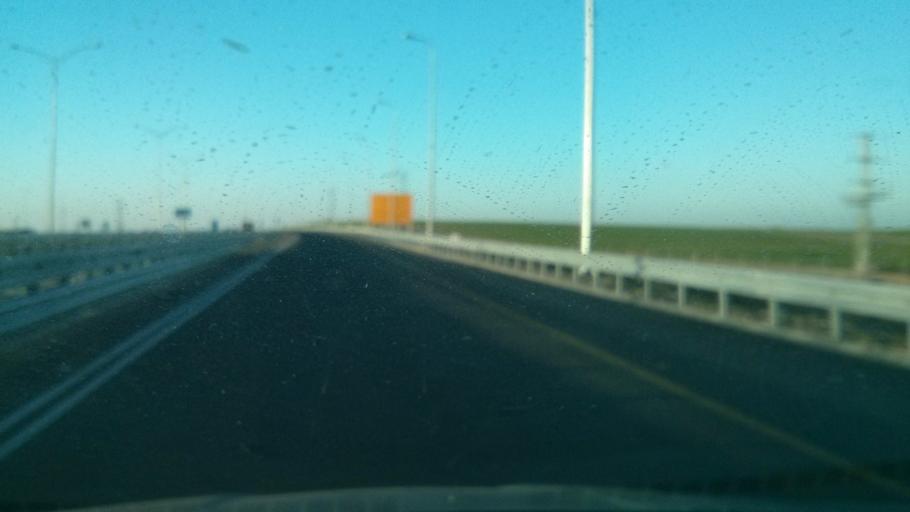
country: IL
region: Southern District
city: Lehavim
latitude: 31.4238
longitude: 34.7851
